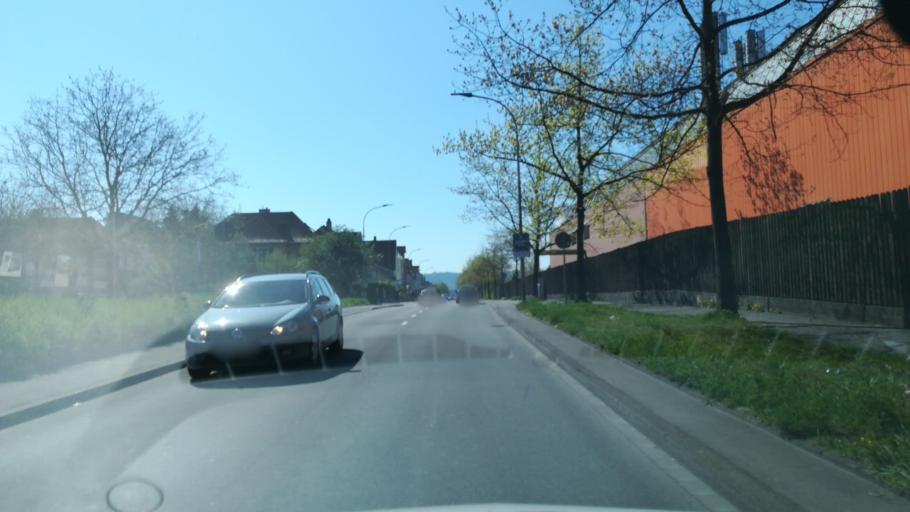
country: DE
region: Baden-Wuerttemberg
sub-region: Freiburg Region
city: Singen
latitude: 47.7591
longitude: 8.8502
